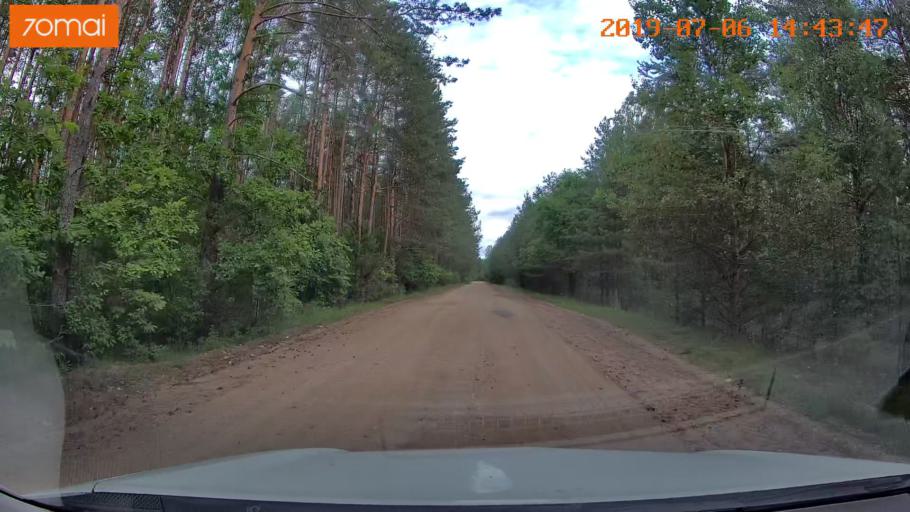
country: BY
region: Minsk
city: Ivyanyets
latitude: 53.9554
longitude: 26.6943
